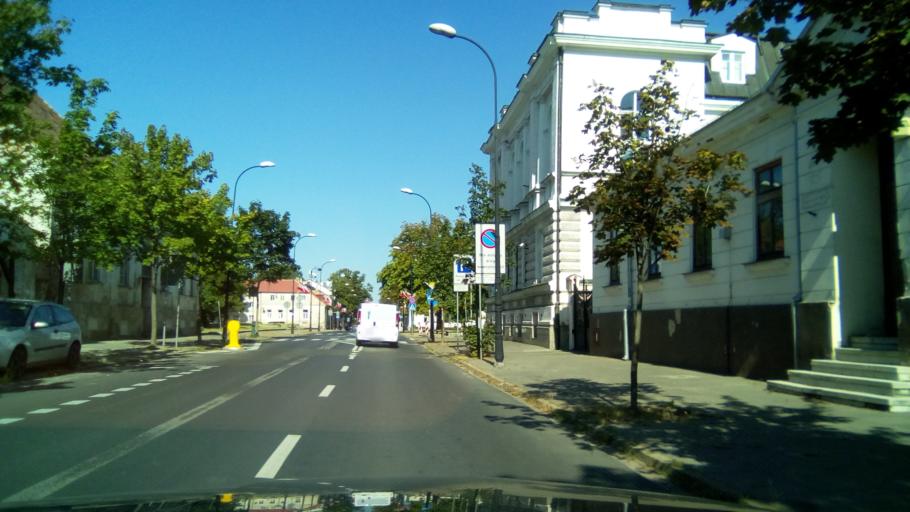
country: PL
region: Masovian Voivodeship
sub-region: Plock
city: Plock
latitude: 52.5412
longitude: 19.6946
